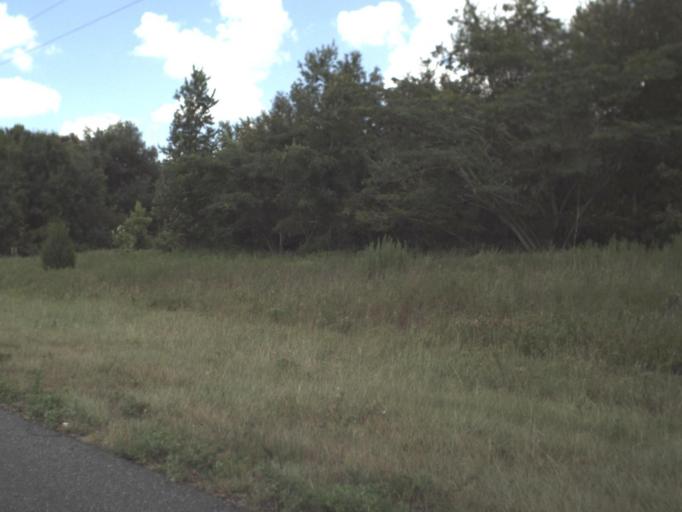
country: US
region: Florida
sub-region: Taylor County
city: Perry
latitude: 30.1710
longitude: -83.6305
